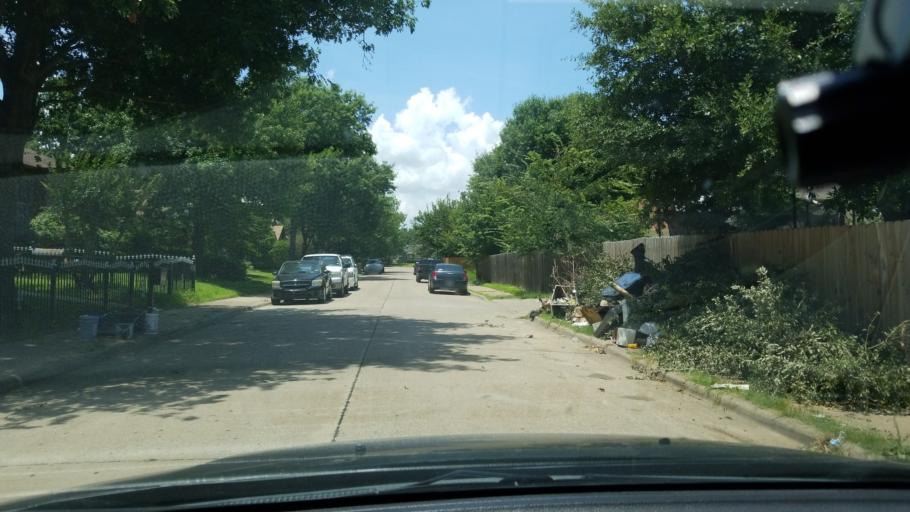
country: US
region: Texas
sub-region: Dallas County
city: Balch Springs
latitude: 32.7514
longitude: -96.6417
